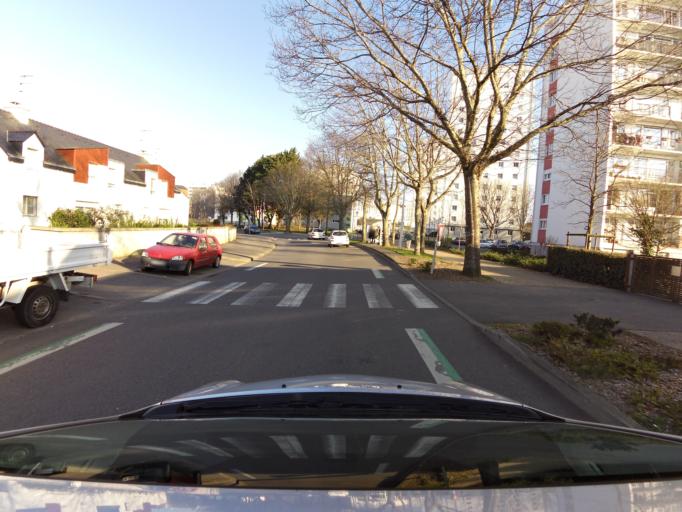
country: FR
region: Brittany
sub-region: Departement du Morbihan
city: Lorient
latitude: 47.7383
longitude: -3.3914
